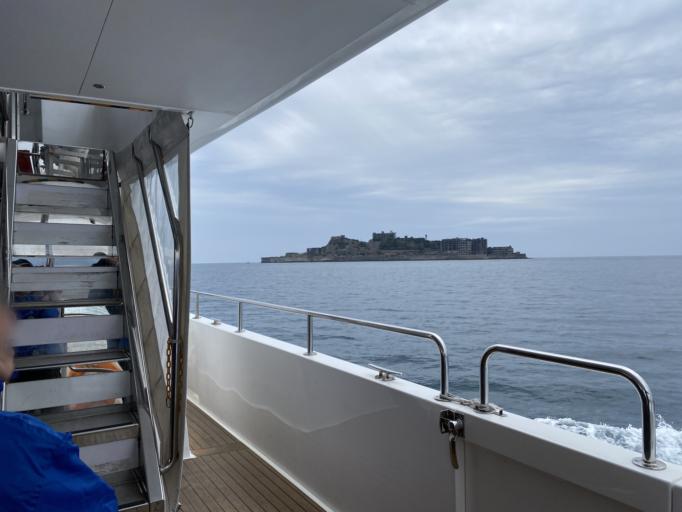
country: JP
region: Nagasaki
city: Nagasaki-shi
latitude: 32.6258
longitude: 129.7477
